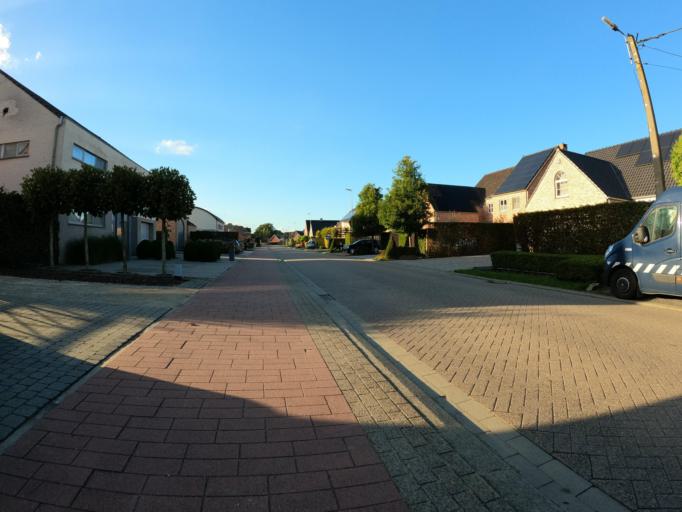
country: BE
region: Flanders
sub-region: Provincie Antwerpen
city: Heist-op-den-Berg
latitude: 51.0417
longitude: 4.7248
